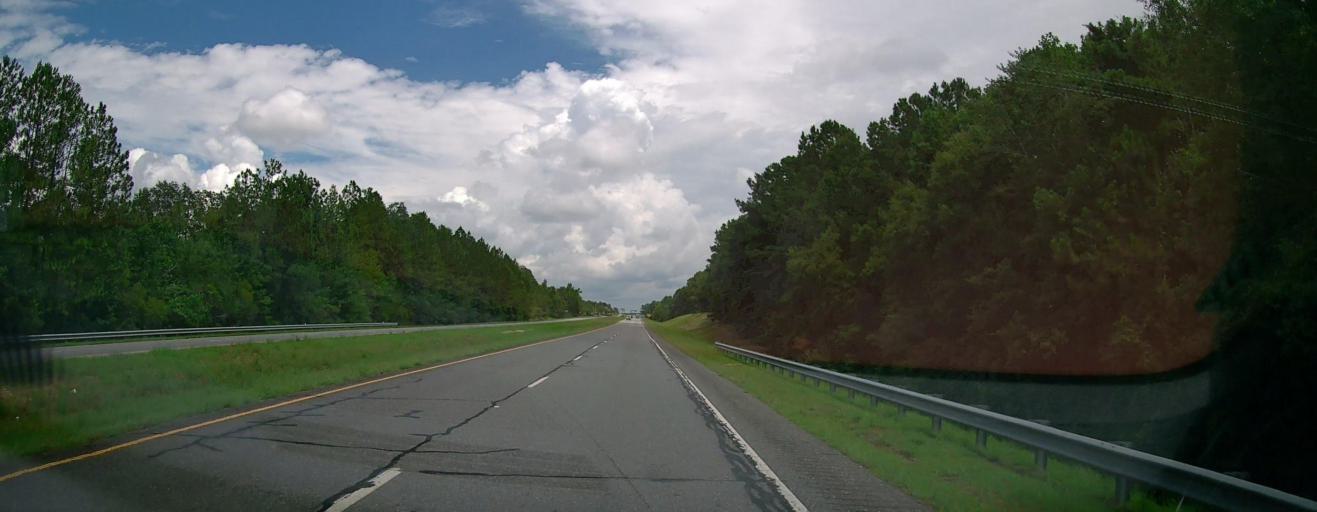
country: US
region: Georgia
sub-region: Dodge County
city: Eastman
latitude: 32.1788
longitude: -83.1887
